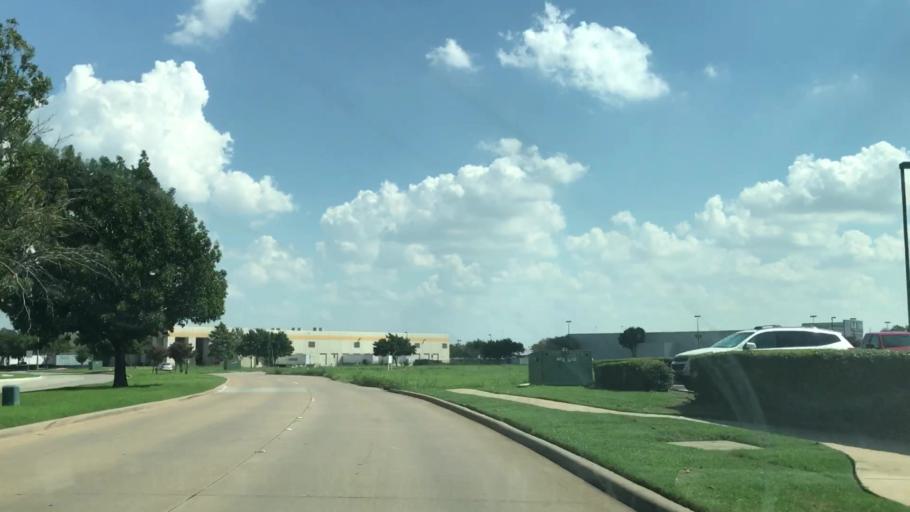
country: US
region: Texas
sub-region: Denton County
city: Lewisville
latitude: 33.0157
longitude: -96.9775
